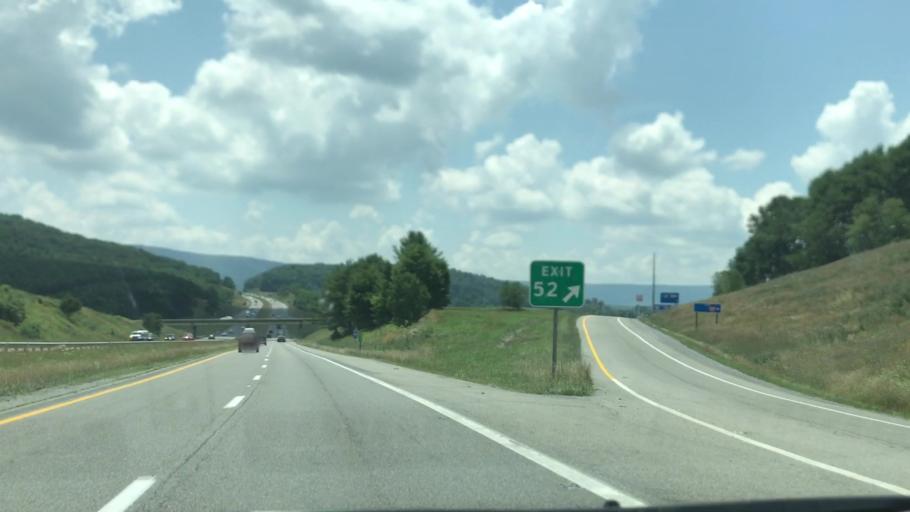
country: US
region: Virginia
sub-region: Bland County
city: Bland
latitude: 37.1042
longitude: -81.1291
